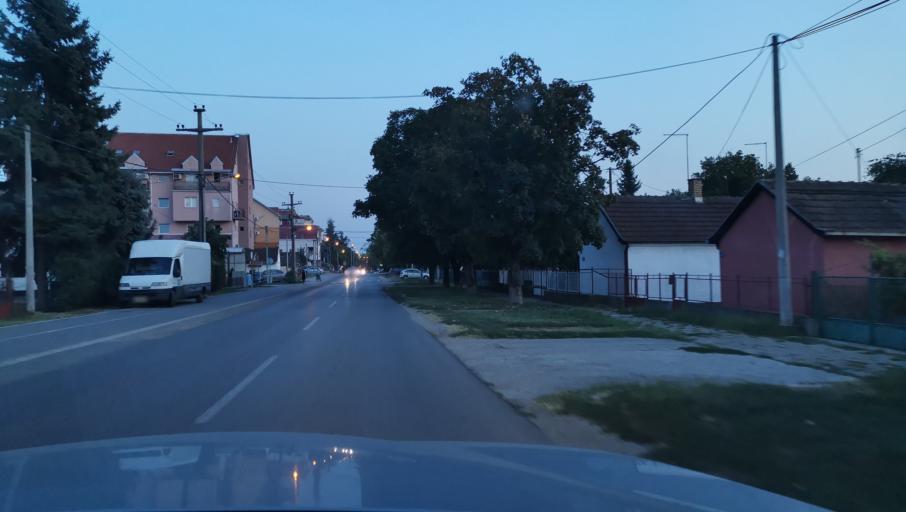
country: RS
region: Central Serbia
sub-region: Belgrade
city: Obrenovac
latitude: 44.6647
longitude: 20.2036
